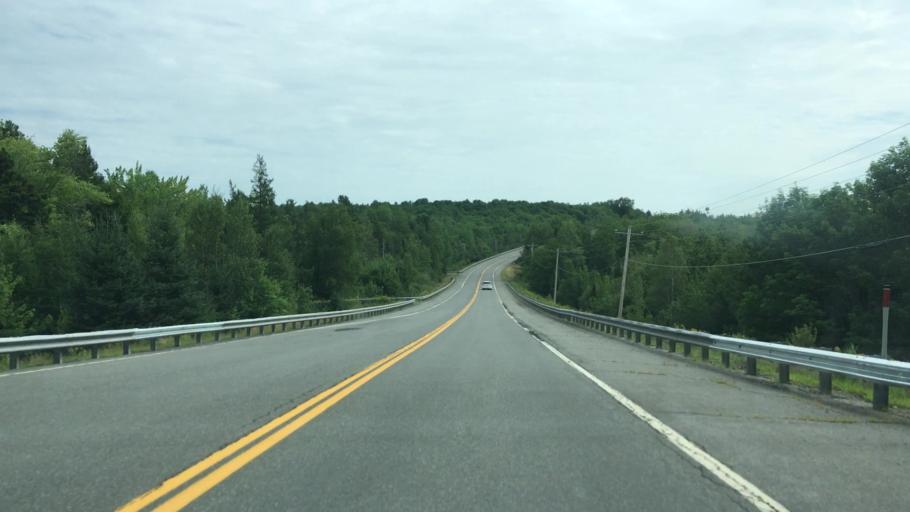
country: US
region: Maine
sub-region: Washington County
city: Calais
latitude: 45.0903
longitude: -67.4895
